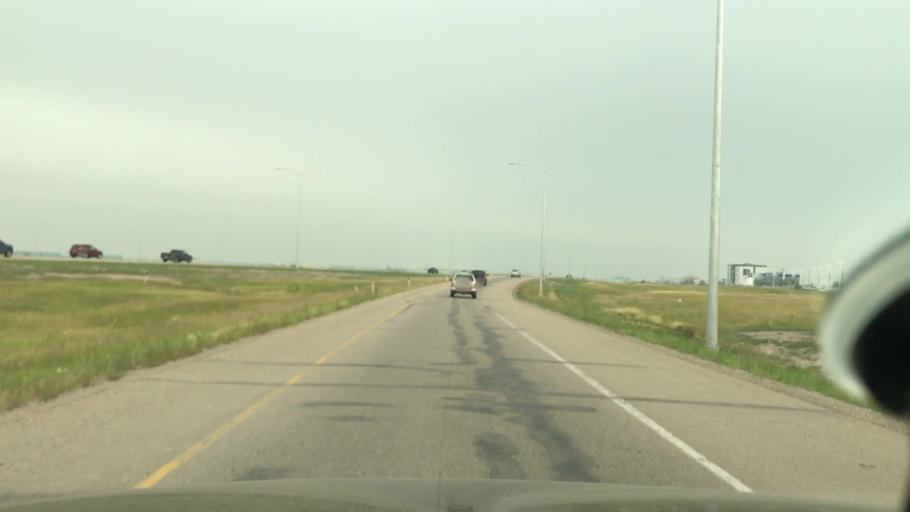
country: CA
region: Alberta
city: Leduc
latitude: 53.2854
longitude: -113.5479
